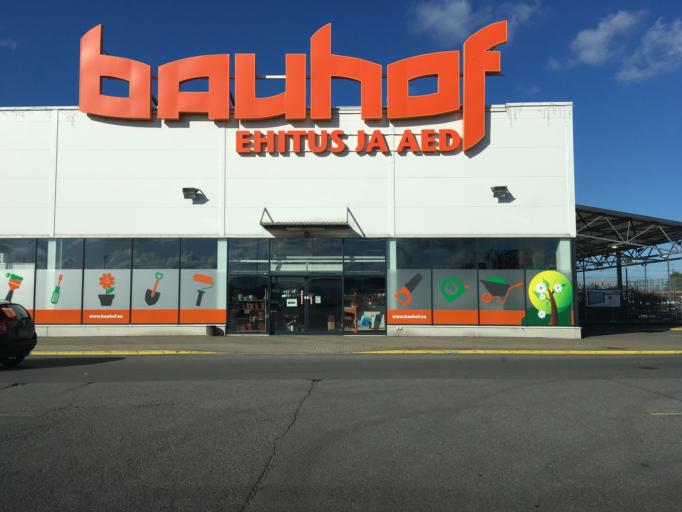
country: EE
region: Harju
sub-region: Saue vald
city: Laagri
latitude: 59.3422
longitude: 24.6154
